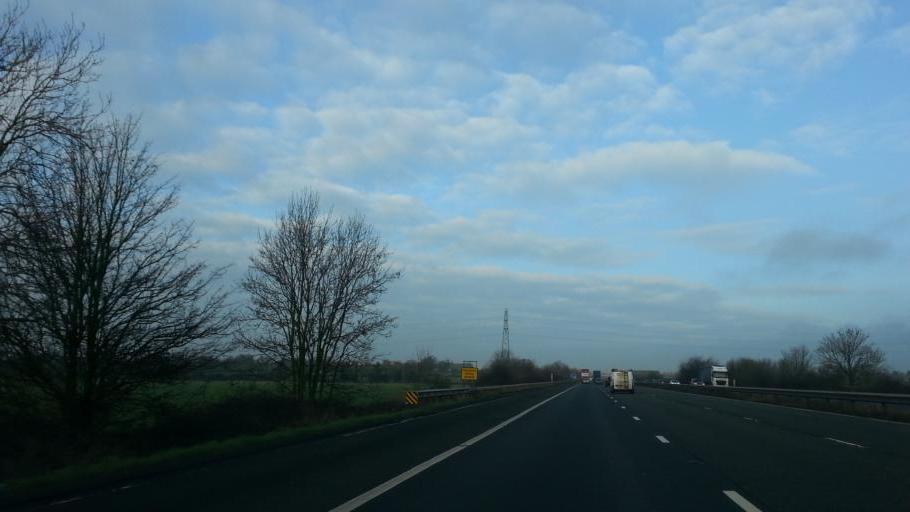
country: GB
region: England
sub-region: Gloucestershire
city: Dursley
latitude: 51.7382
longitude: -2.3424
